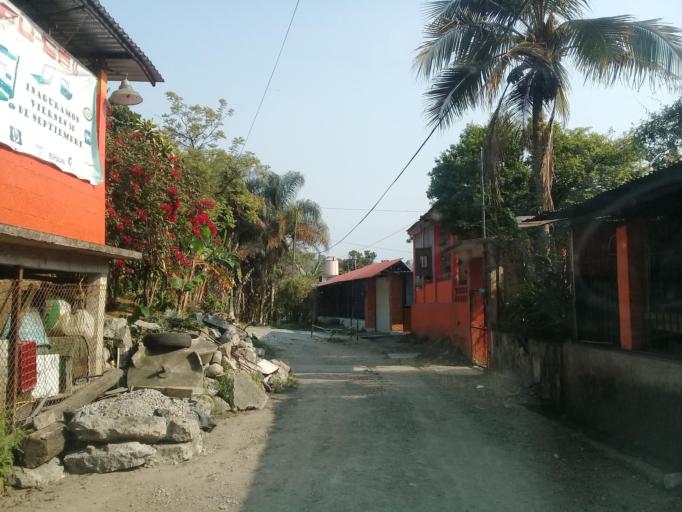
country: MX
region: Veracruz
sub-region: Ixtaczoquitlan
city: Campo Chico
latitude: 18.8511
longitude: -97.0384
